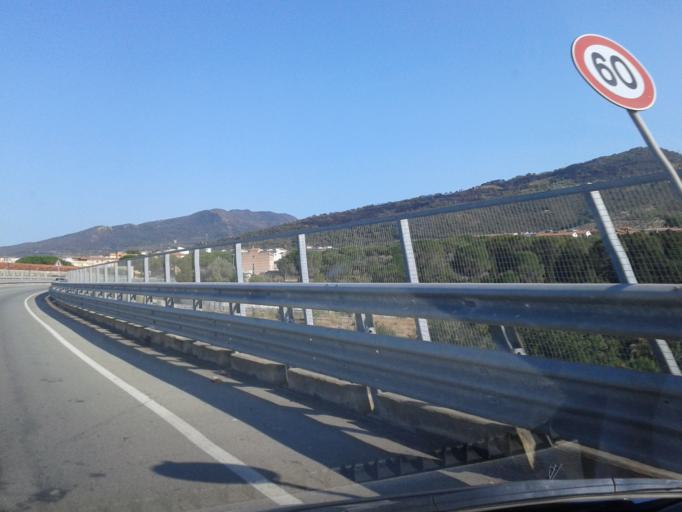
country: IT
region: Sicily
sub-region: Palermo
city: Finale
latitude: 38.0225
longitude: 14.1550
